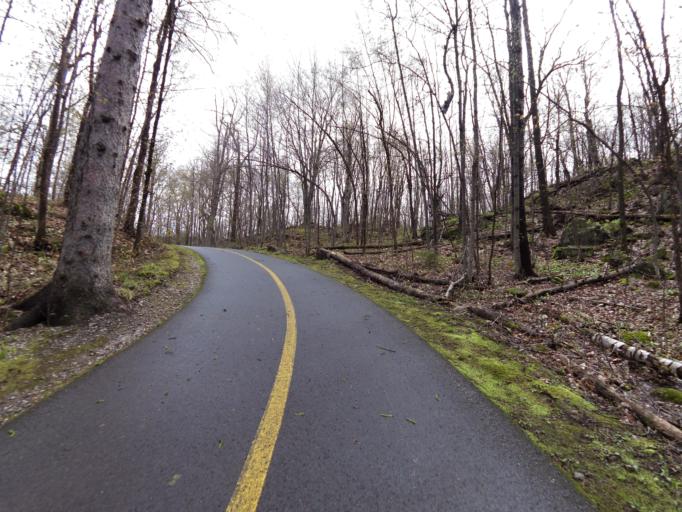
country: CA
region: Quebec
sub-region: Outaouais
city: Gatineau
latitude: 45.4655
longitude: -75.7798
